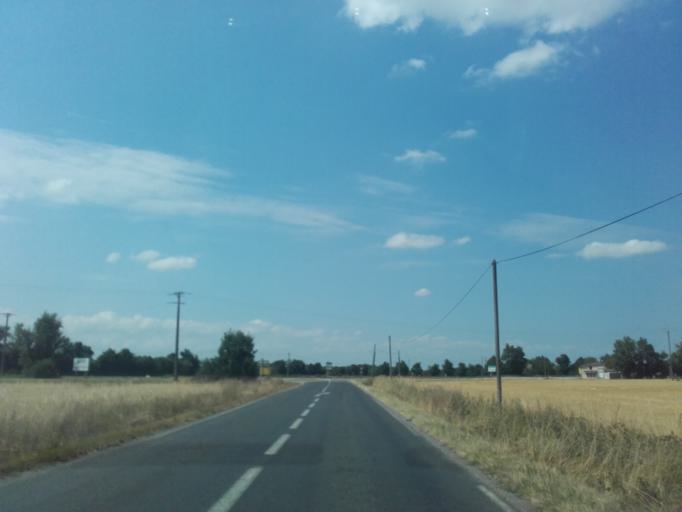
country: FR
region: Rhone-Alpes
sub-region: Departement de l'Ain
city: Villars-les-Dombes
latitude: 46.0472
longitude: 5.0714
